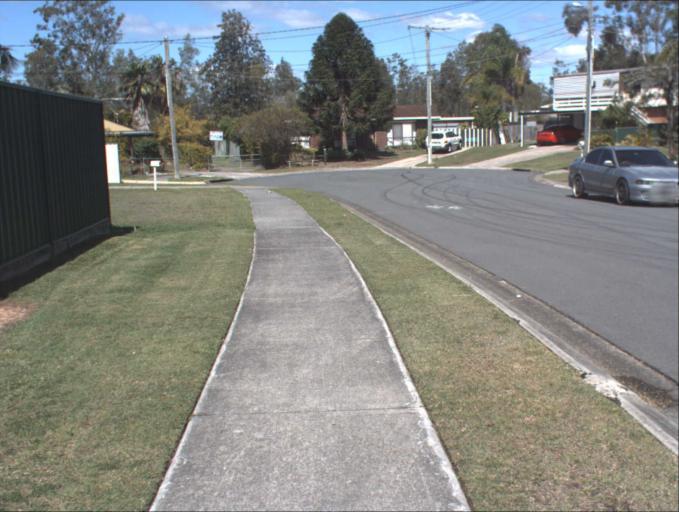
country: AU
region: Queensland
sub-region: Logan
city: Logan Reserve
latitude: -27.6906
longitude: 153.0882
